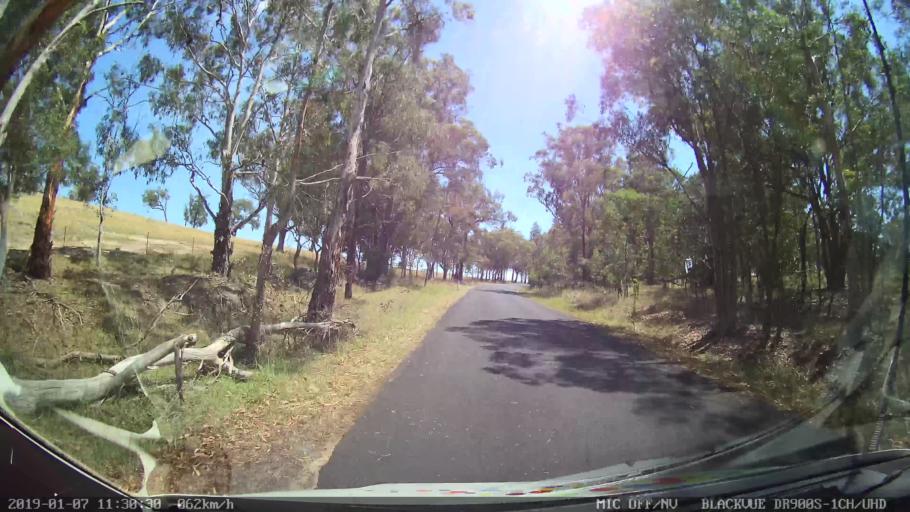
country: AU
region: New South Wales
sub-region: Armidale Dumaresq
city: Armidale
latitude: -30.4286
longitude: 151.5632
